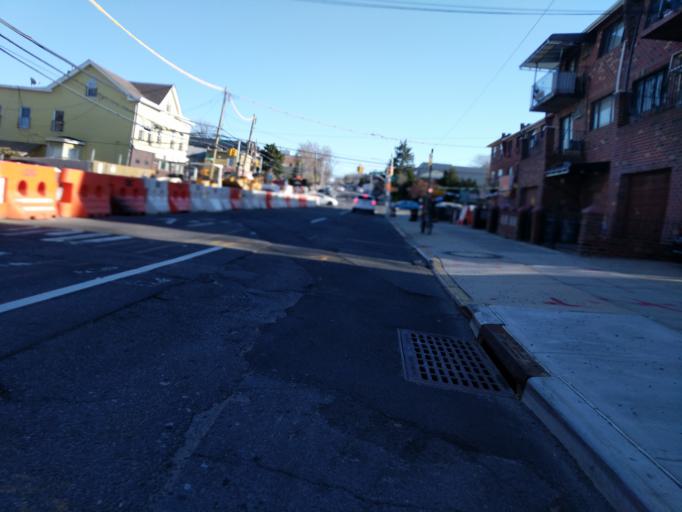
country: US
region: New York
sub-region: Queens County
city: Long Island City
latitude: 40.7358
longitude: -73.8961
